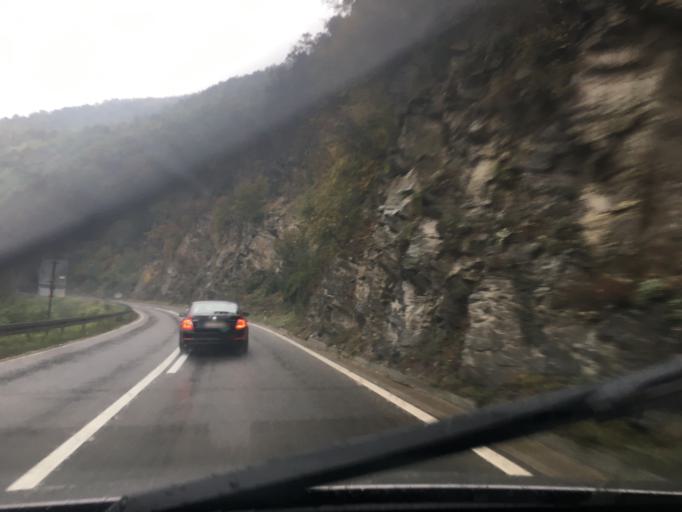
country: RS
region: Central Serbia
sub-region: Pcinjski Okrug
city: Vladicin Han
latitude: 42.7303
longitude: 22.0665
